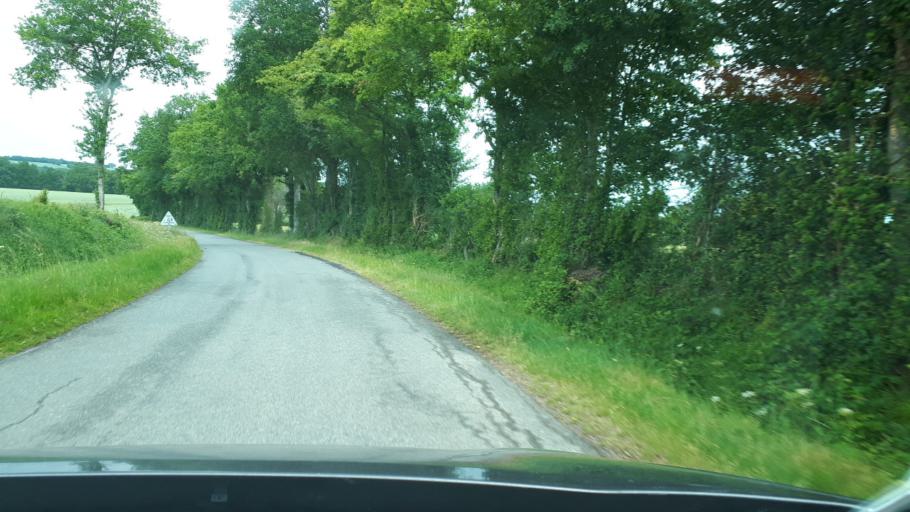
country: FR
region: Centre
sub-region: Departement du Cher
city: Henrichemont
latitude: 47.4061
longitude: 2.6407
